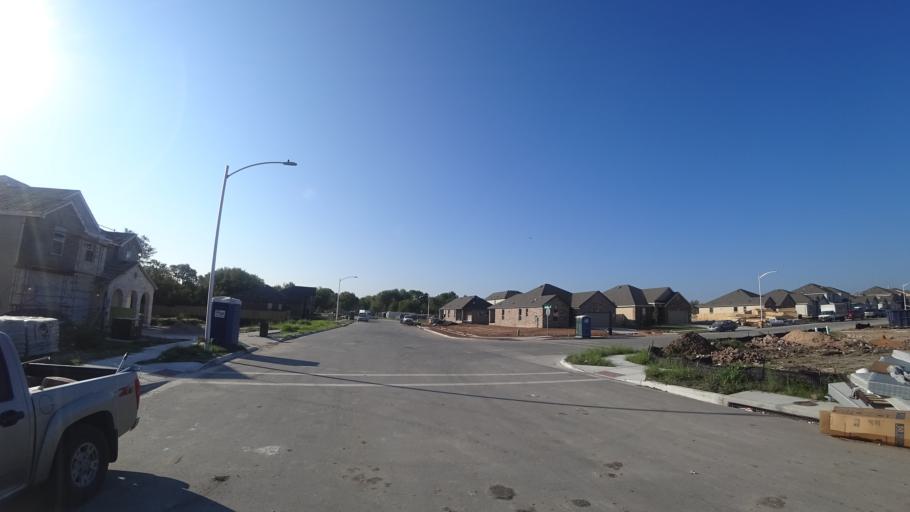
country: US
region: Texas
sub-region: Travis County
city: Manor
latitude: 30.3177
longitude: -97.6532
